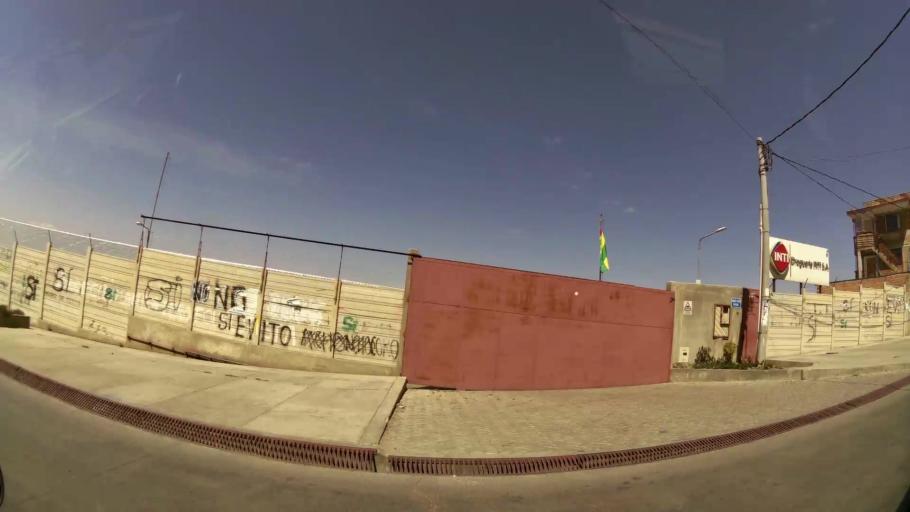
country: BO
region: La Paz
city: La Paz
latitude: -16.5305
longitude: -68.1447
